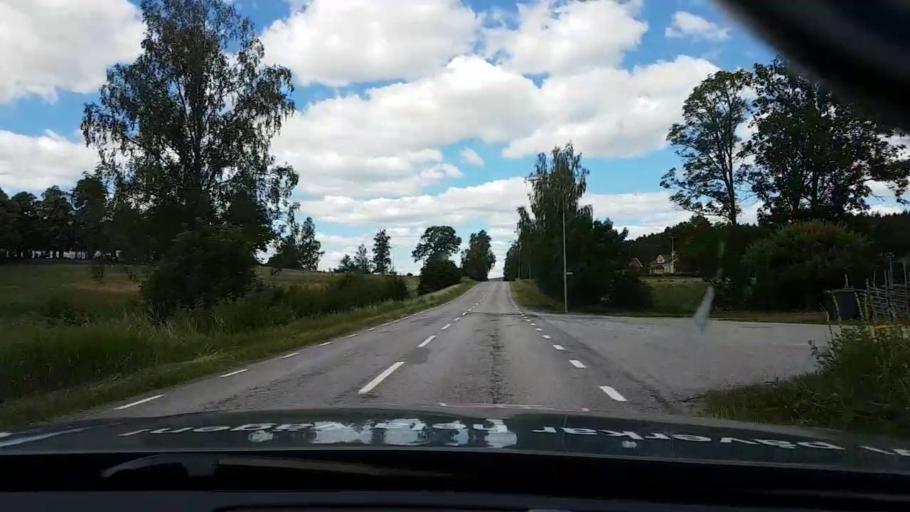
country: SE
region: Kalmar
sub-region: Vasterviks Kommun
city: Overum
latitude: 58.0787
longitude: 16.3559
